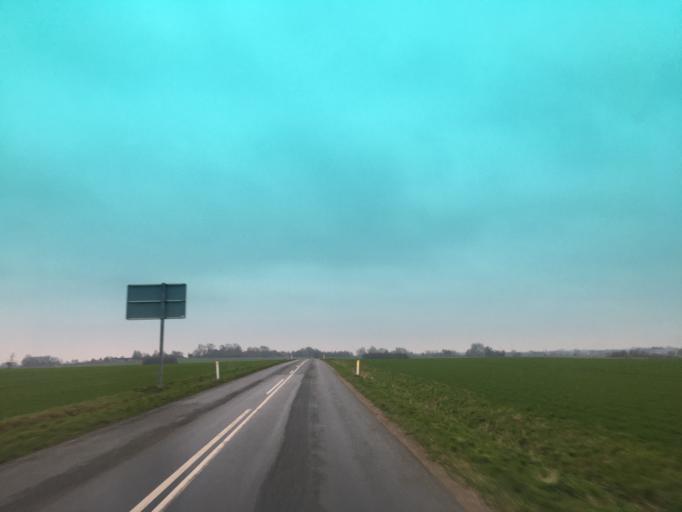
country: DK
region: Zealand
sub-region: Slagelse Kommune
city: Skaelskor
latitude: 55.2939
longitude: 11.3934
